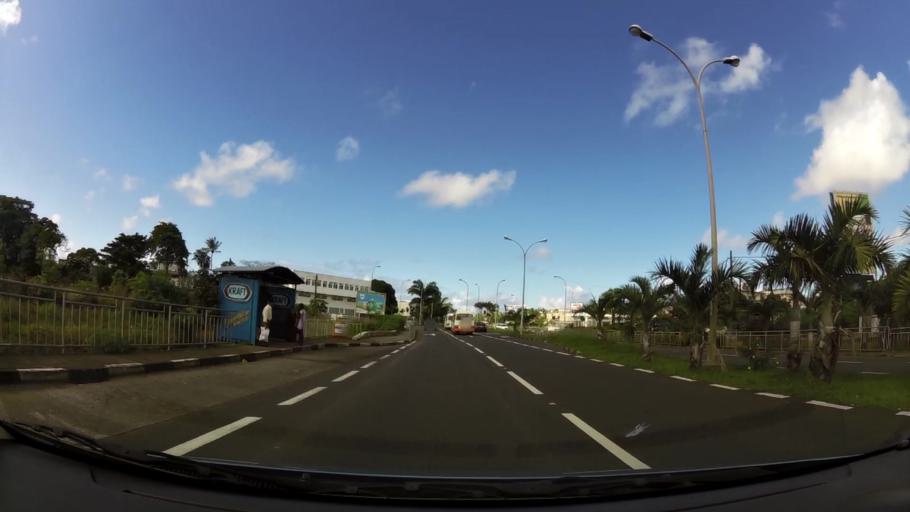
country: MU
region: Grand Port
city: Plaine Magnien
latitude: -20.4290
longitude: 57.6660
